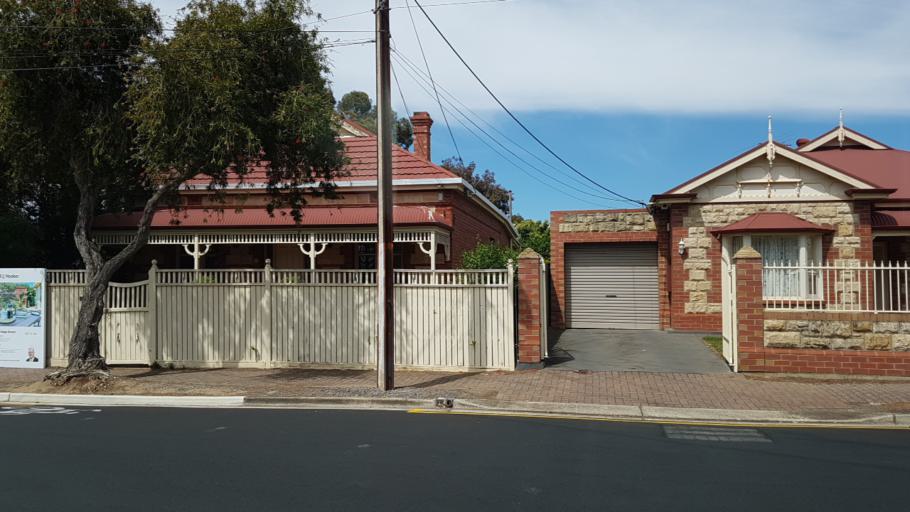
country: AU
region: South Australia
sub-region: Norwood Payneham St Peters
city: Trinity Gardens
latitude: -34.9119
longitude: 138.6514
